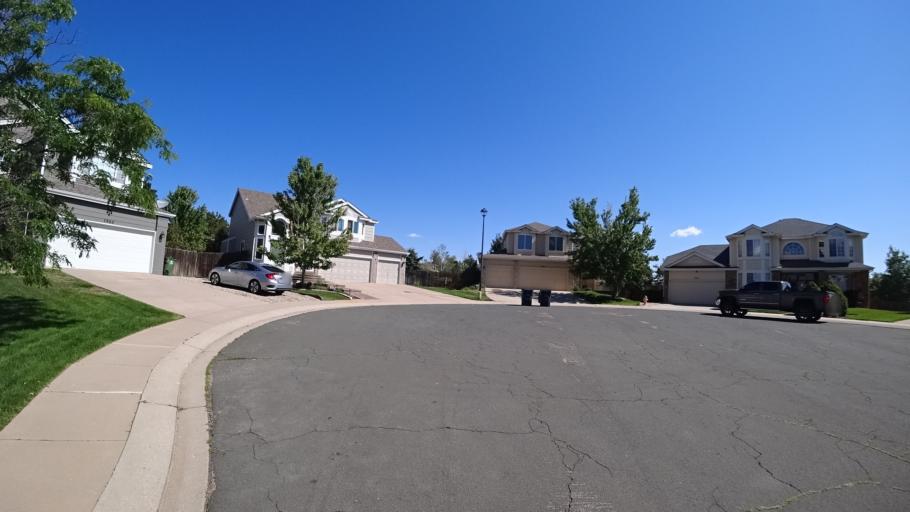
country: US
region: Colorado
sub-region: El Paso County
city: Black Forest
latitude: 38.9463
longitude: -104.7458
